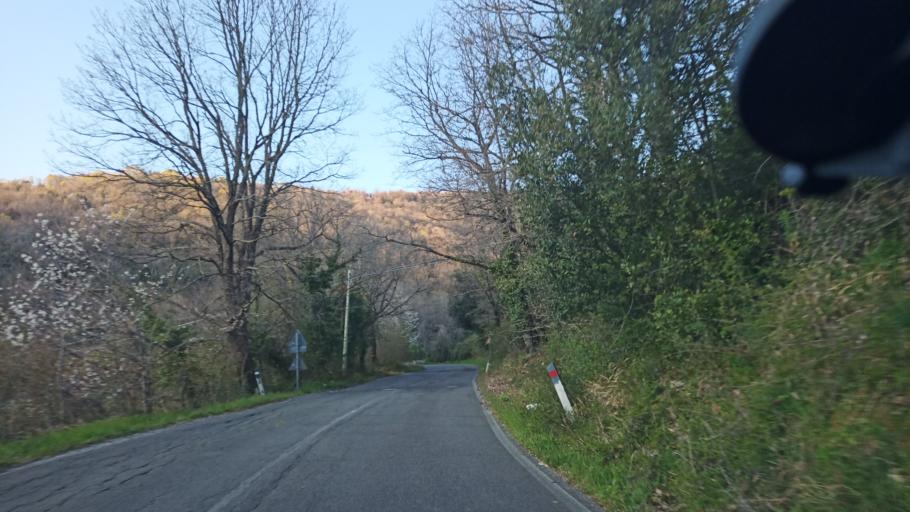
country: IT
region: Latium
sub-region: Provincia di Rieti
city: Cottanello
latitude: 42.4097
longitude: 12.6813
